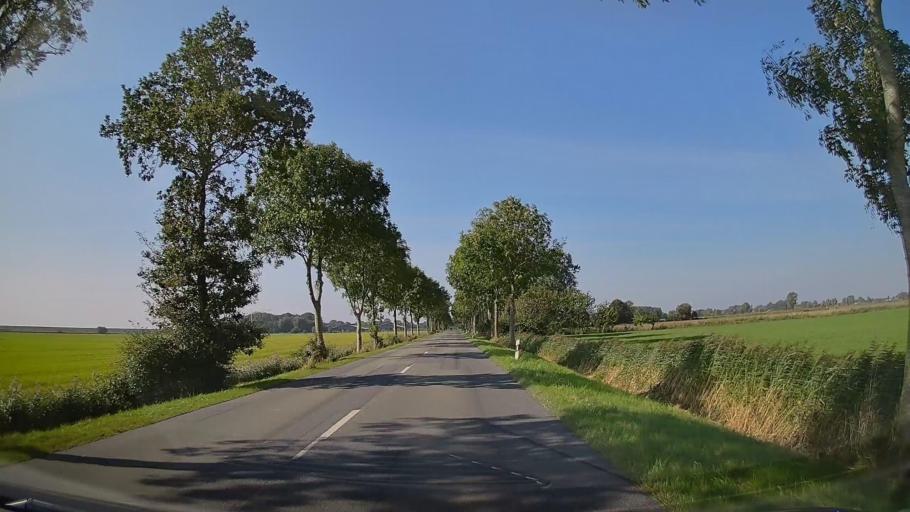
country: DE
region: Lower Saxony
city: Wremen
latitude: 53.6261
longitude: 8.5237
